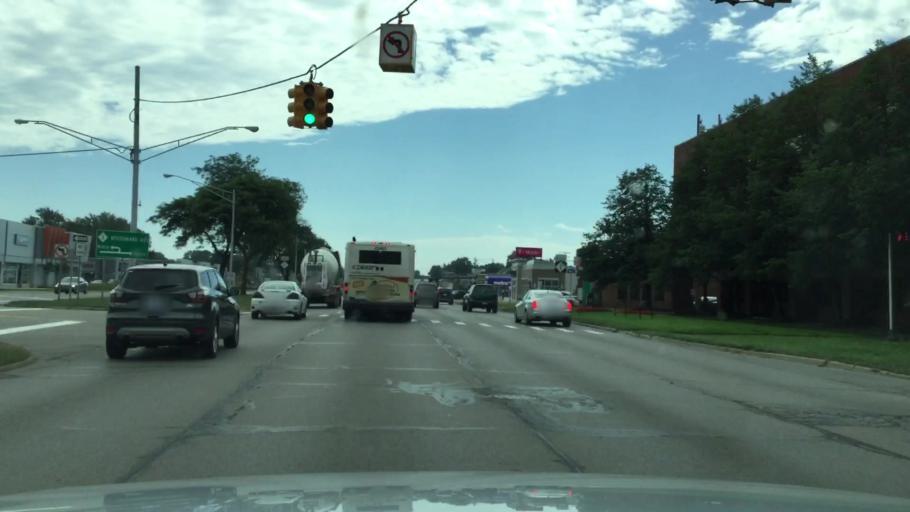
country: US
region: Michigan
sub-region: Oakland County
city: Huntington Woods
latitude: 42.4967
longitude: -83.1659
